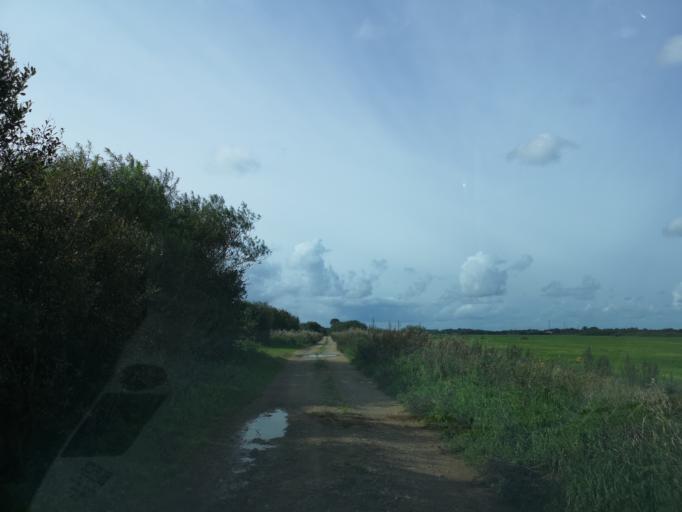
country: DK
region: Central Jutland
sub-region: Ringkobing-Skjern Kommune
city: Tarm
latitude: 55.9305
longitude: 8.5326
